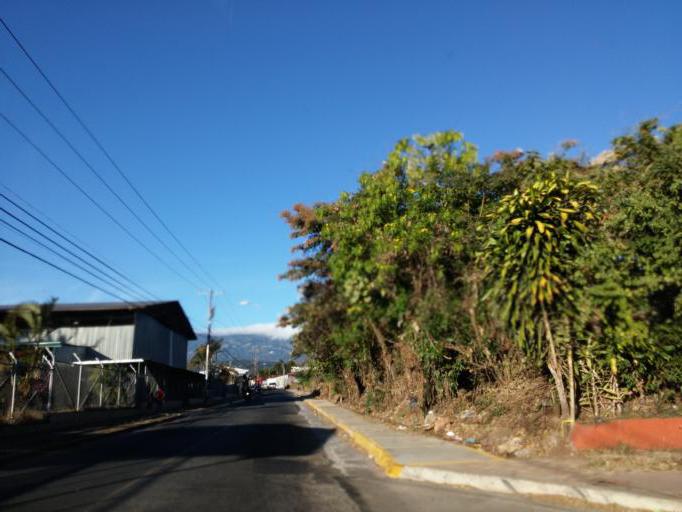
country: CR
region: Alajuela
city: Alajuela
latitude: 10.0090
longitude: -84.2031
